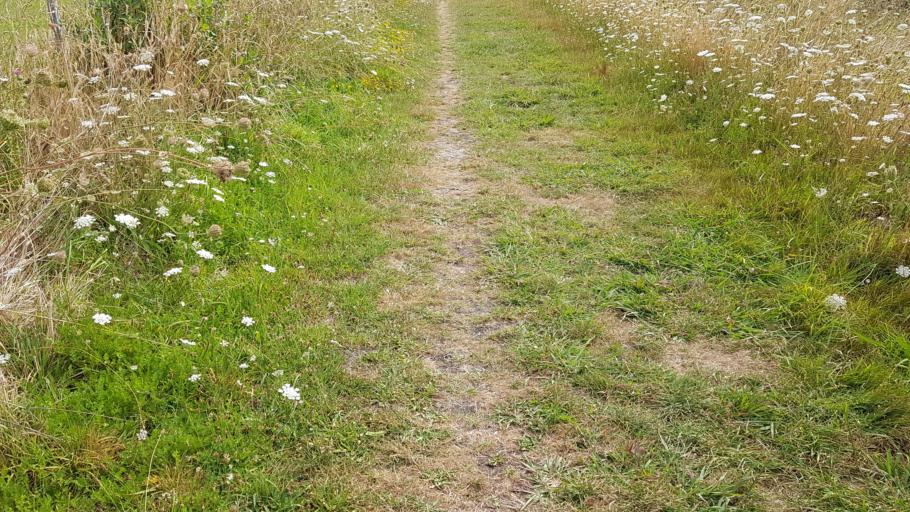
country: NZ
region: Auckland
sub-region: Auckland
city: Rothesay Bay
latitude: -36.6618
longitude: 174.7428
